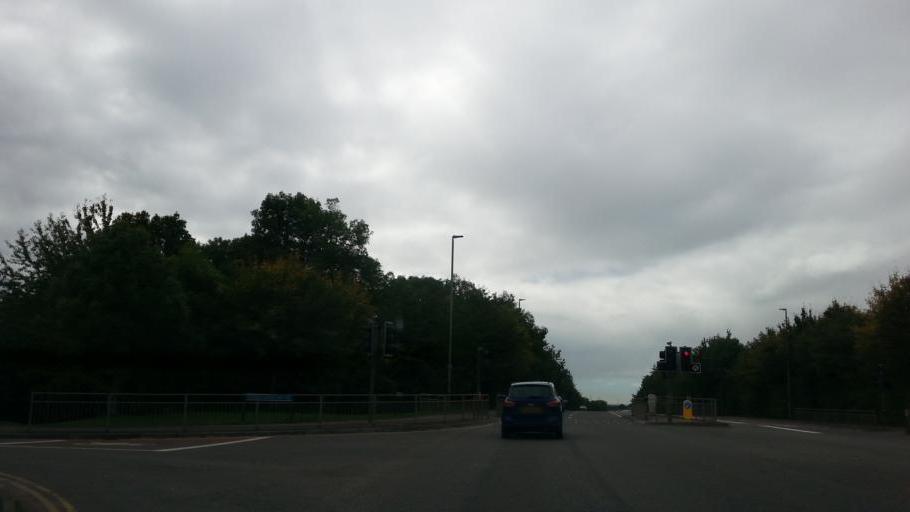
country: GB
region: England
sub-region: Gloucestershire
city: Gloucester
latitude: 51.8499
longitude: -2.2633
